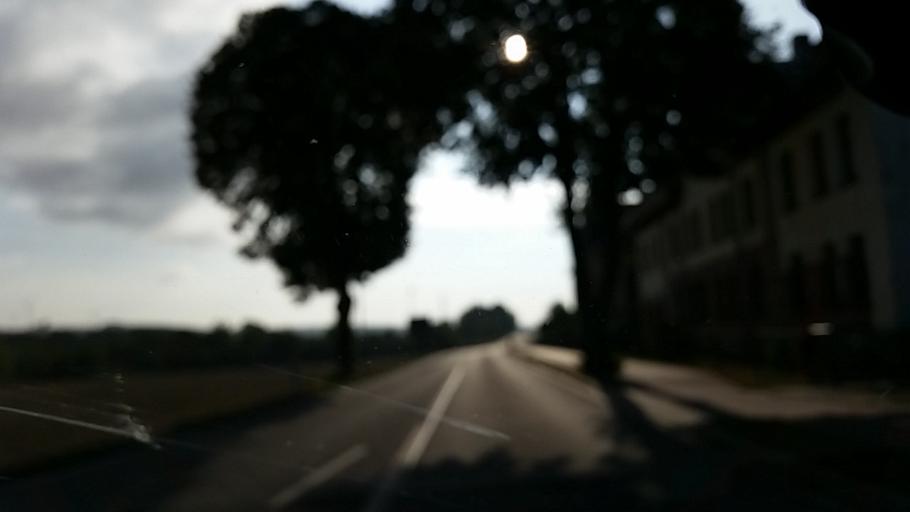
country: DE
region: Thuringia
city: Kleinfurra
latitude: 51.4146
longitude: 10.7541
